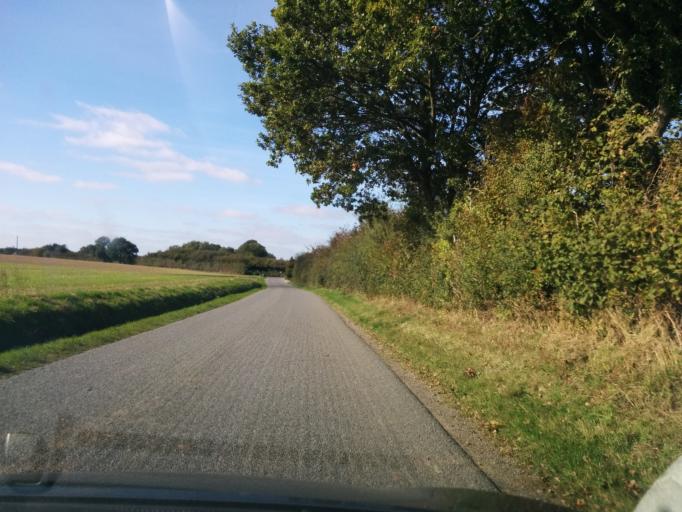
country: DK
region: South Denmark
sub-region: Kolding Kommune
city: Sonder Bjert
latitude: 55.4042
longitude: 9.5543
